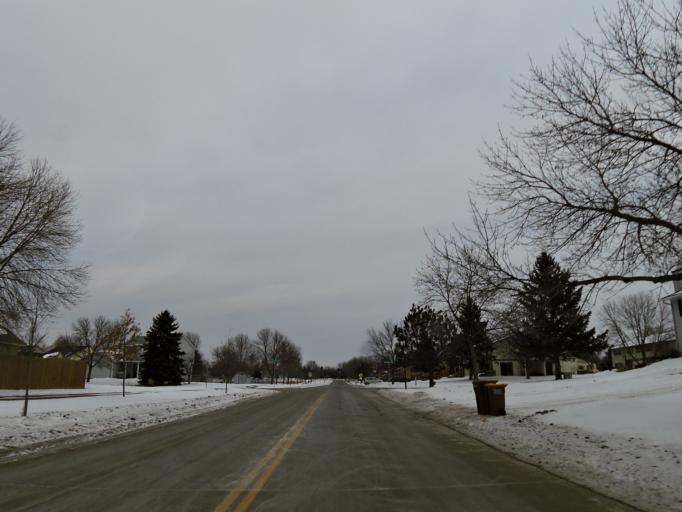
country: US
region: Minnesota
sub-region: Washington County
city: Woodbury
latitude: 44.9078
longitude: -92.9209
